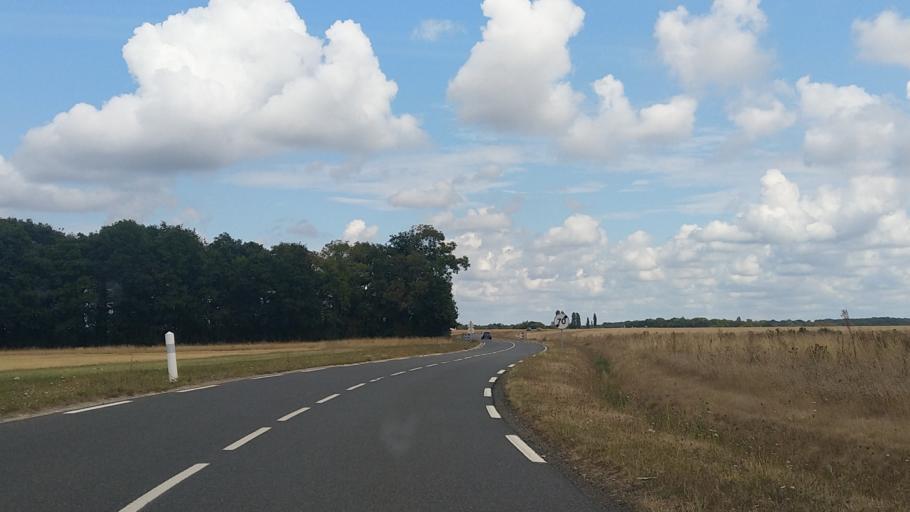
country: FR
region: Ile-de-France
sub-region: Departement des Yvelines
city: Sonchamp
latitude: 48.5799
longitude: 1.8433
